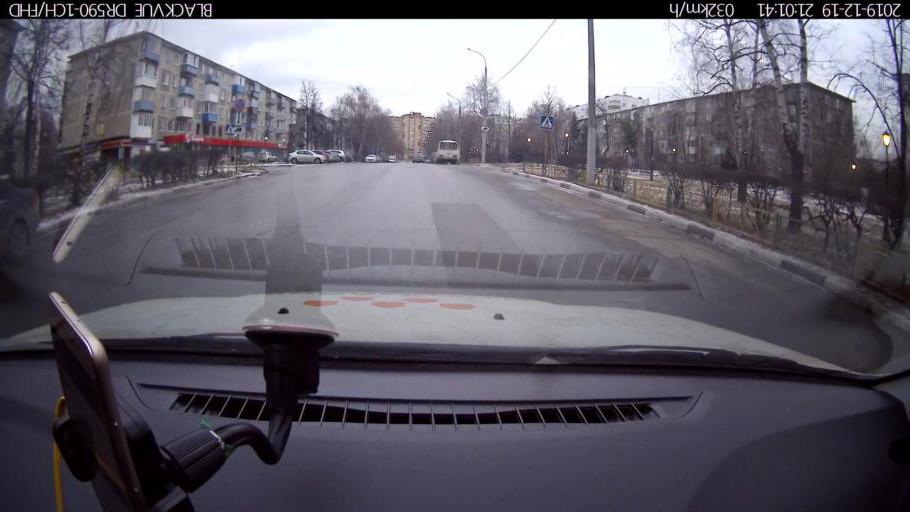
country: RU
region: Nizjnij Novgorod
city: Gorbatovka
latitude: 56.3466
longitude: 43.8530
